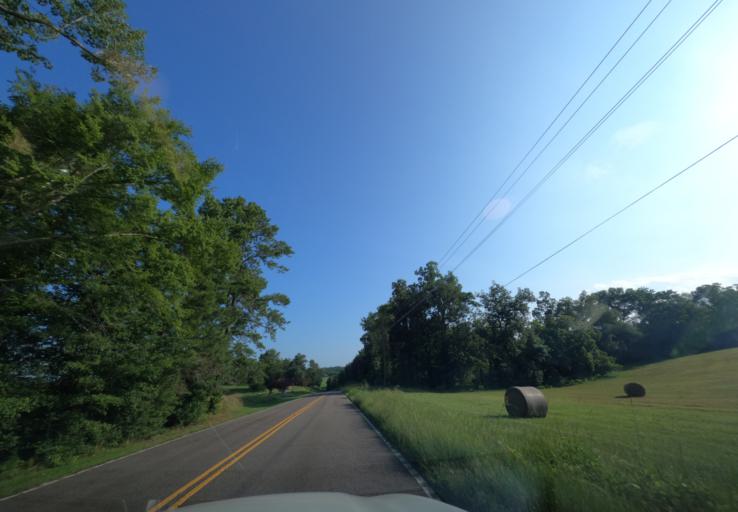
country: US
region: South Carolina
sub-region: Edgefield County
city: Murphys Estates
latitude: 33.6576
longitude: -81.9737
